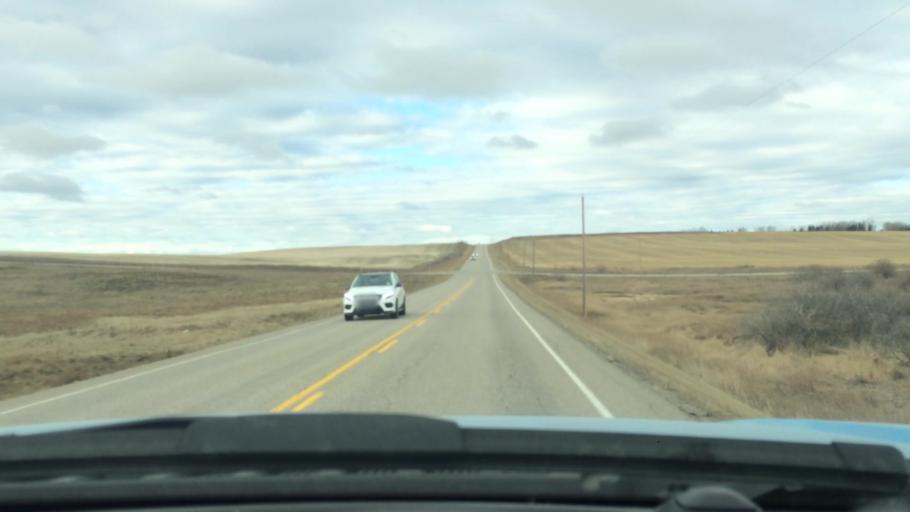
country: CA
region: Alberta
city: Airdrie
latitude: 51.2124
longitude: -114.1150
